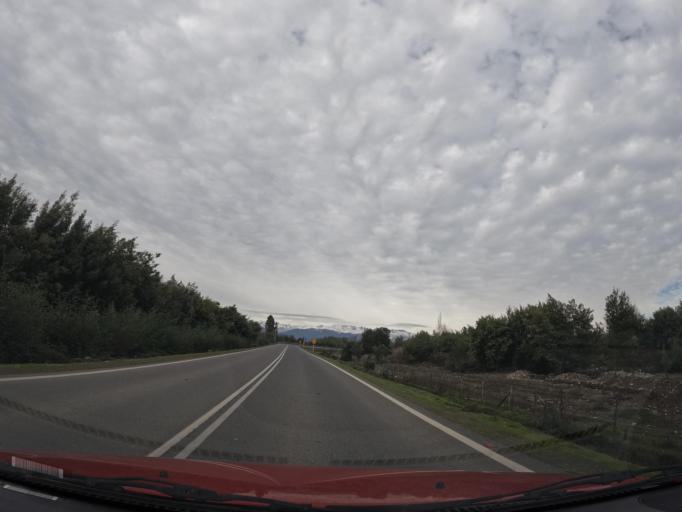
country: CL
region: Maule
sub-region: Provincia de Linares
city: Linares
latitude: -35.9078
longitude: -71.4937
